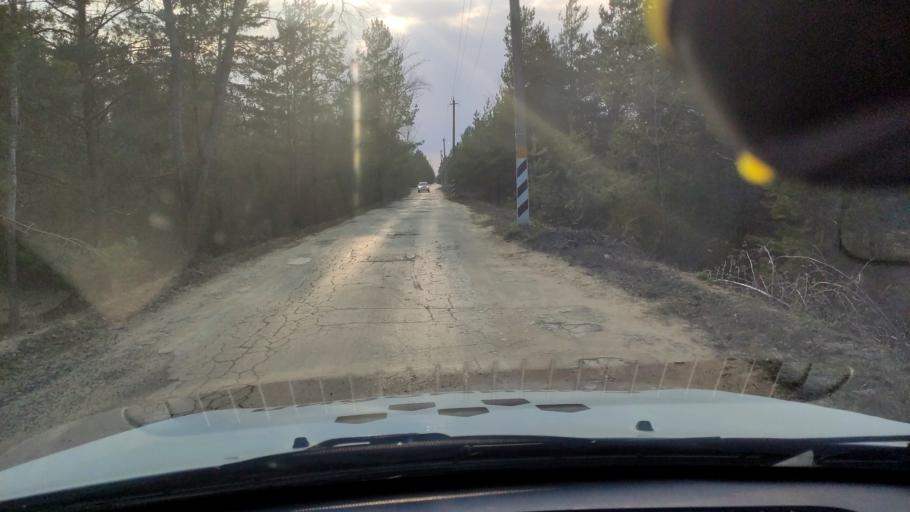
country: RU
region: Samara
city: Zhigulevsk
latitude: 53.4587
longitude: 49.6215
